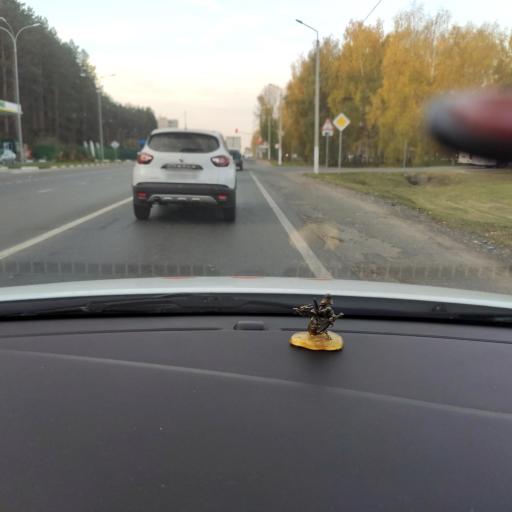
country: RU
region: Tatarstan
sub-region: Zelenodol'skiy Rayon
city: Zelenodolsk
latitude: 55.8525
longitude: 48.5695
